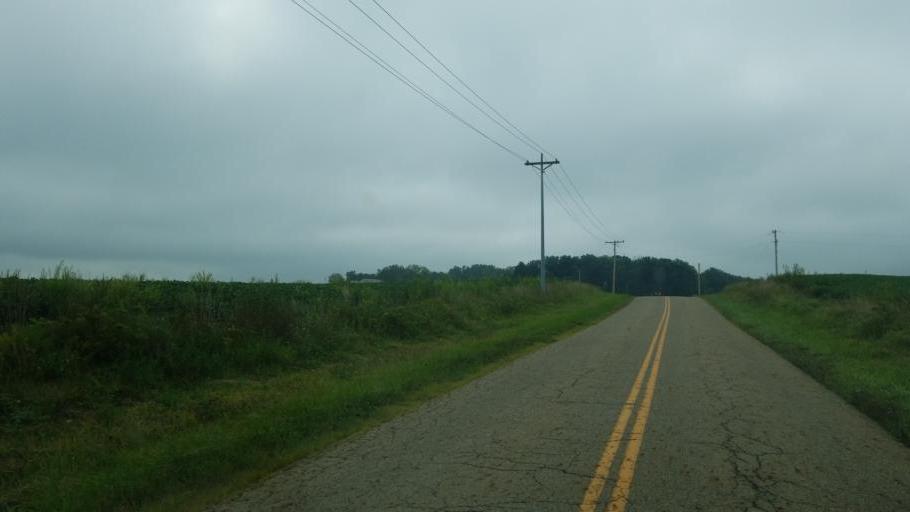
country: US
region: Ohio
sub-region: Licking County
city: Utica
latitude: 40.2909
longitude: -82.4309
